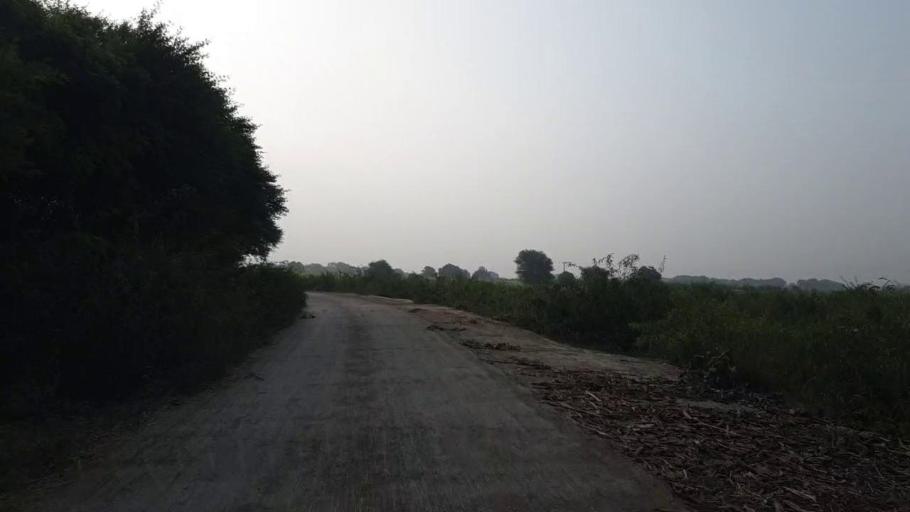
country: PK
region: Sindh
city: Tando Muhammad Khan
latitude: 25.1704
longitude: 68.6070
